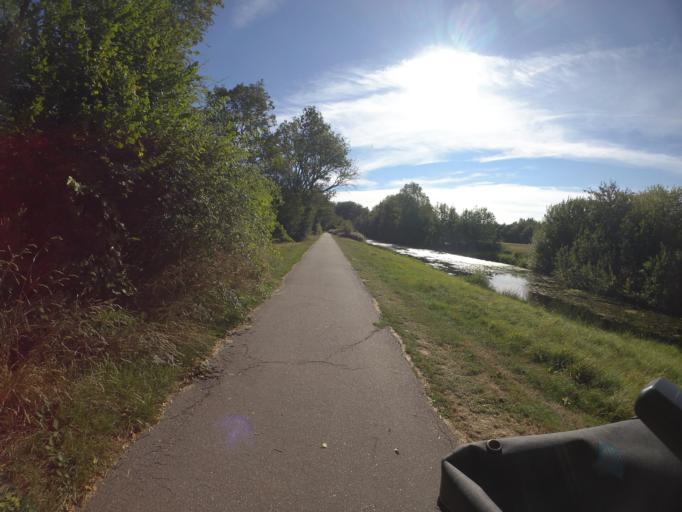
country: NL
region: Drenthe
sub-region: Gemeente Hoogeveen
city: Hoogeveen
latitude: 52.7112
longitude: 6.4807
